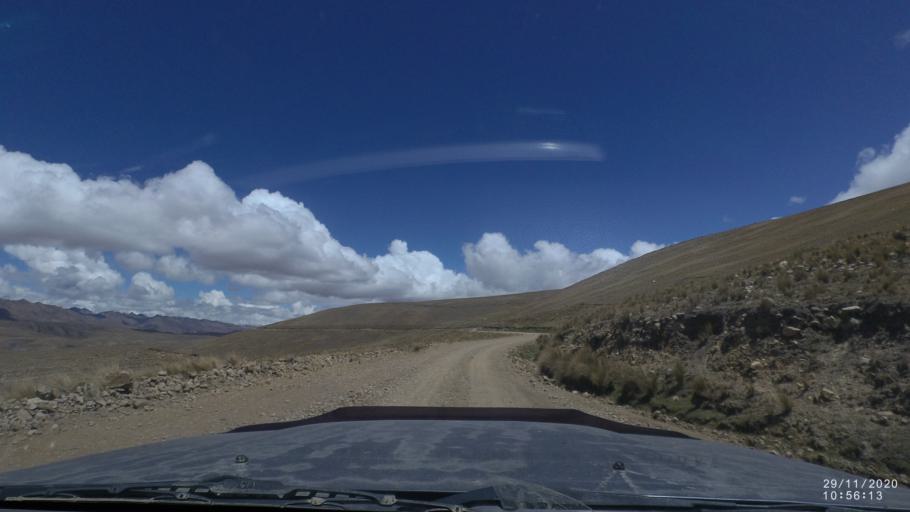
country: BO
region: Cochabamba
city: Cochabamba
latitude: -17.2212
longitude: -66.2241
